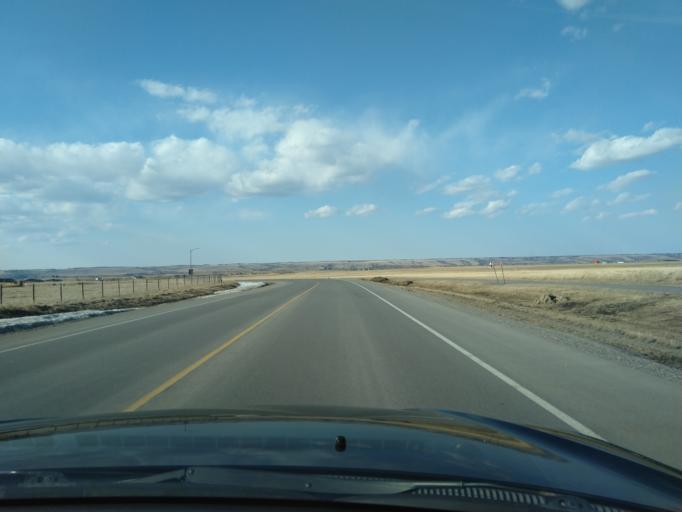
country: CA
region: Alberta
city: Cochrane
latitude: 51.1008
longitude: -114.3885
